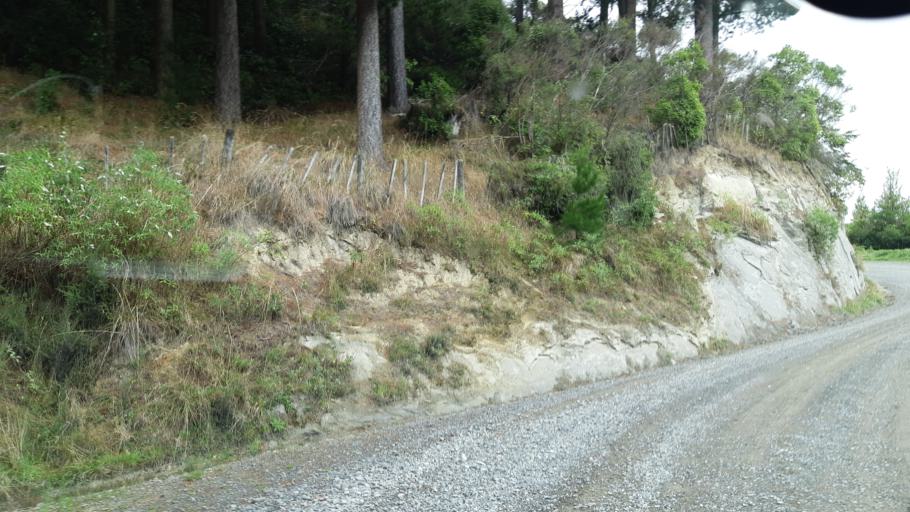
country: NZ
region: Manawatu-Wanganui
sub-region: Ruapehu District
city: Waiouru
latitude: -39.7813
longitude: 175.6826
